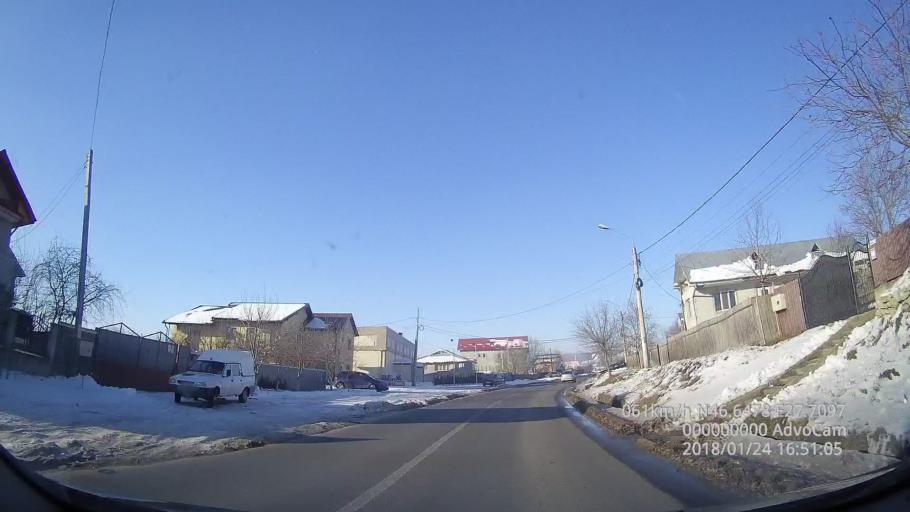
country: RO
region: Vaslui
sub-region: Municipiul Vaslui
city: Rediu
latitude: 46.6480
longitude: 27.7095
